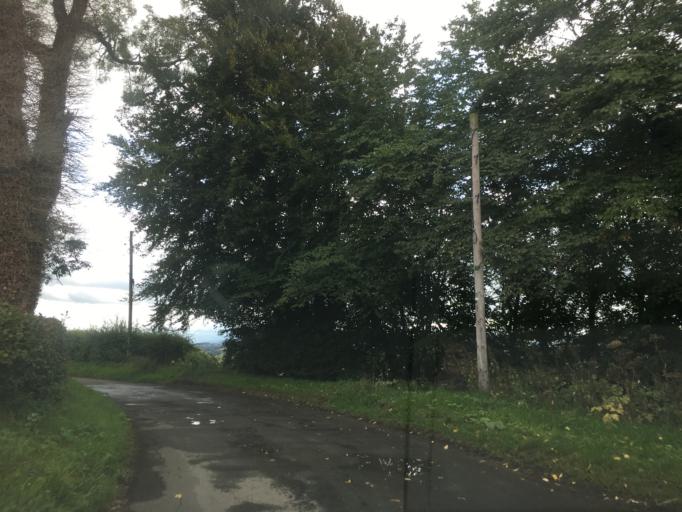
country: GB
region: Scotland
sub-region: Falkirk
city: Bo'ness
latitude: 55.9957
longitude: -3.6425
